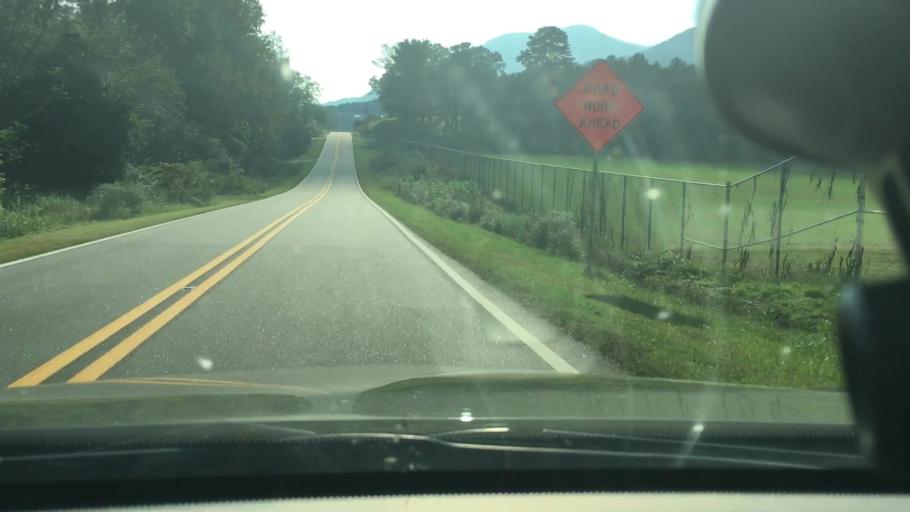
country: US
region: North Carolina
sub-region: Polk County
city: Columbus
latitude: 35.3003
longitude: -82.1577
